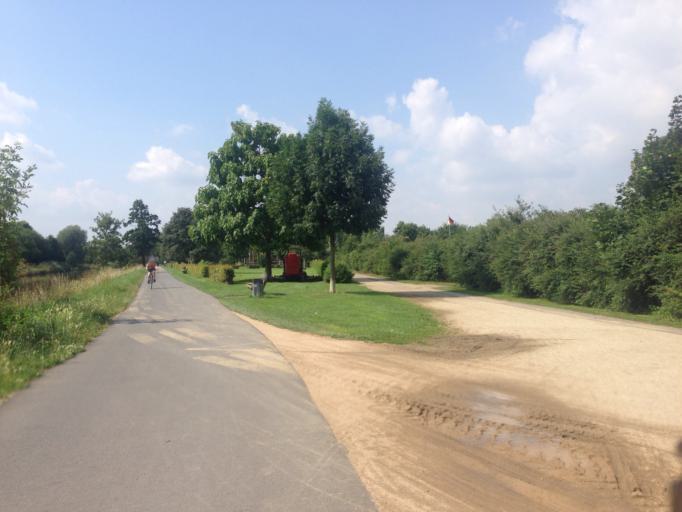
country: DE
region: Hesse
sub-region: Regierungsbezirk Darmstadt
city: Frankfurt am Main
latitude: 50.1532
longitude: 8.6442
